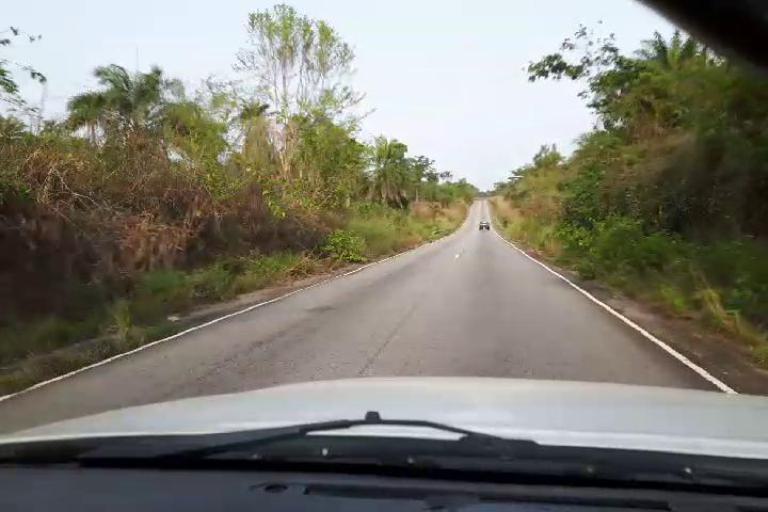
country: SL
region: Southern Province
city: Baoma
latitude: 7.9243
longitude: -11.5411
